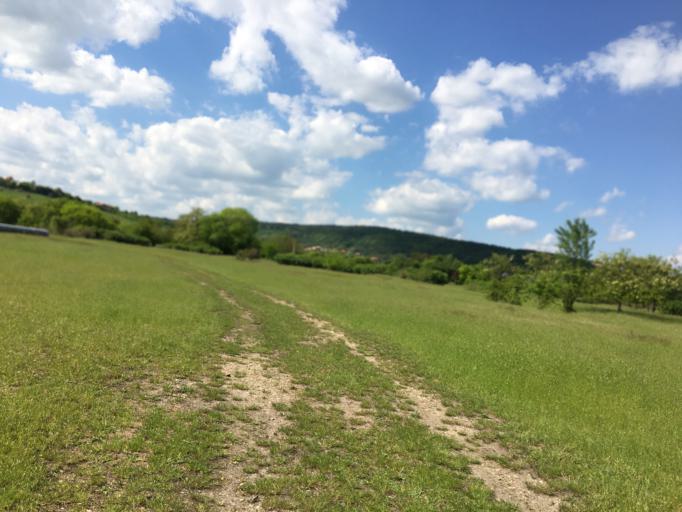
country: HU
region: Pest
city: Urom
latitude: 47.5722
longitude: 19.0348
